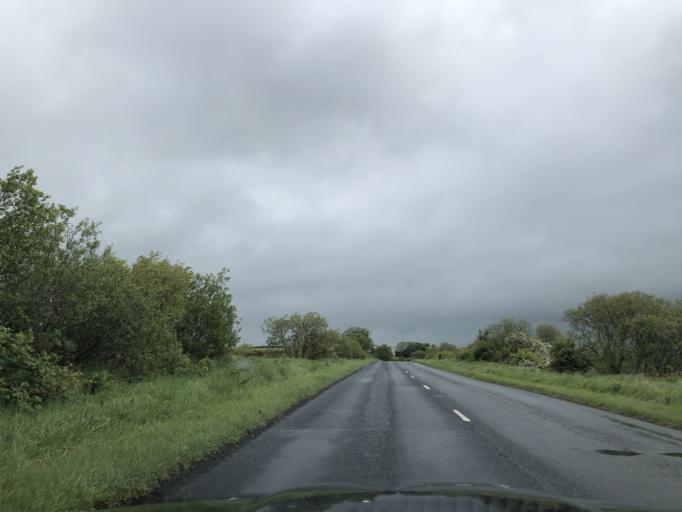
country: GB
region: Northern Ireland
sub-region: Moyle District
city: Ballycastle
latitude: 55.1669
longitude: -6.3601
